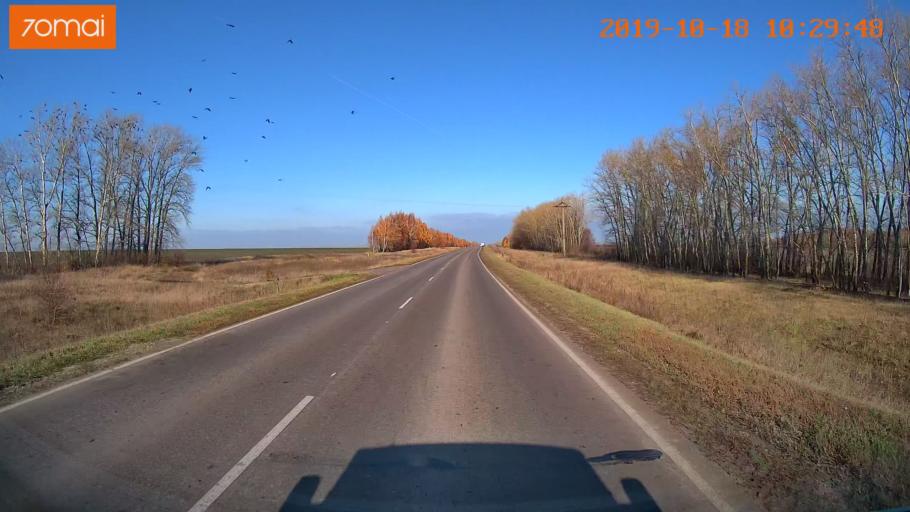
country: RU
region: Tula
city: Kurkino
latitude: 53.4562
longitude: 38.6519
